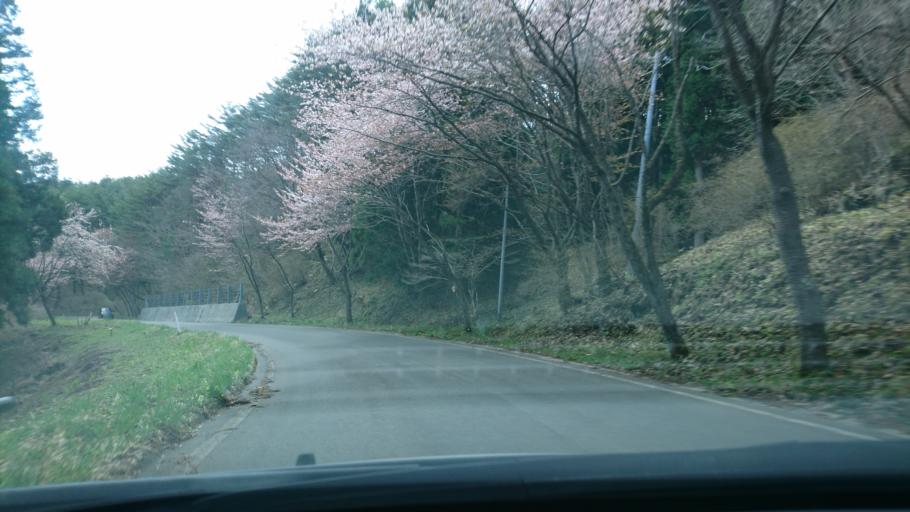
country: JP
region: Iwate
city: Ofunato
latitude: 38.9655
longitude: 141.4465
